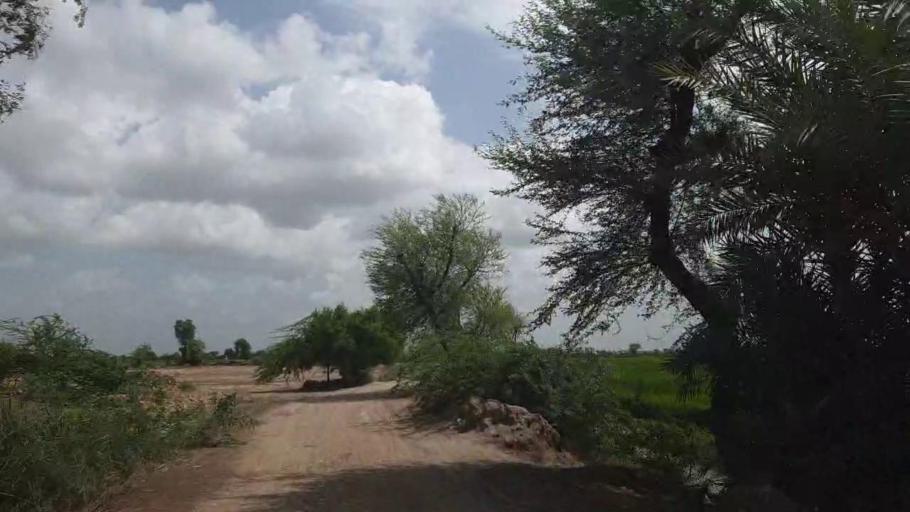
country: PK
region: Sindh
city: Tando Bago
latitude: 24.6544
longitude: 68.9983
